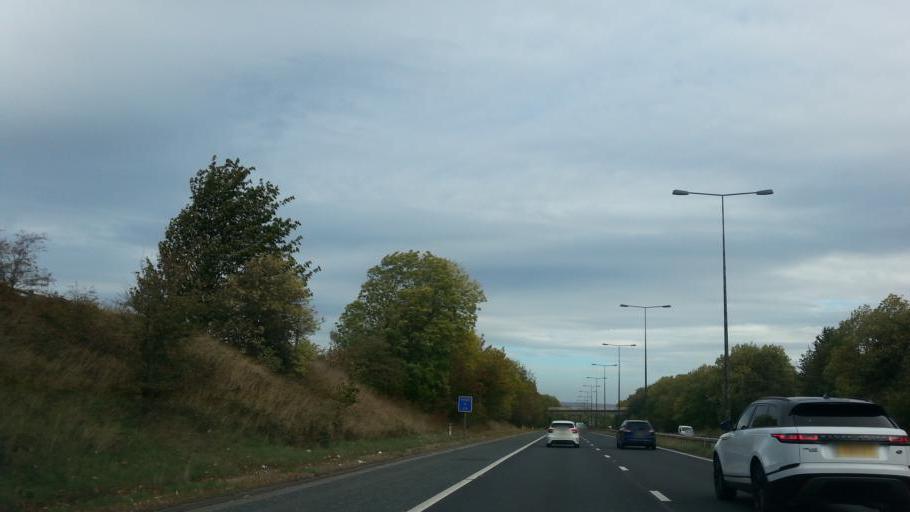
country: GB
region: England
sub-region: City and Borough of Leeds
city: Gildersome
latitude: 53.7513
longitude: -1.6173
